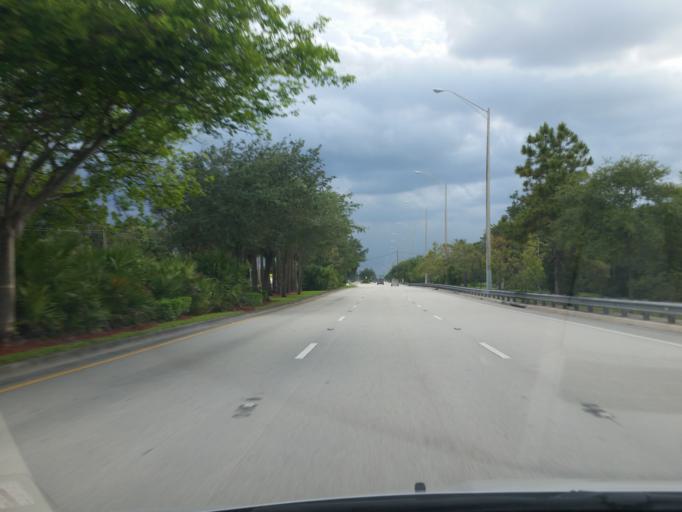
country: US
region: Florida
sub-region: Broward County
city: Davie
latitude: 26.0650
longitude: -80.2412
